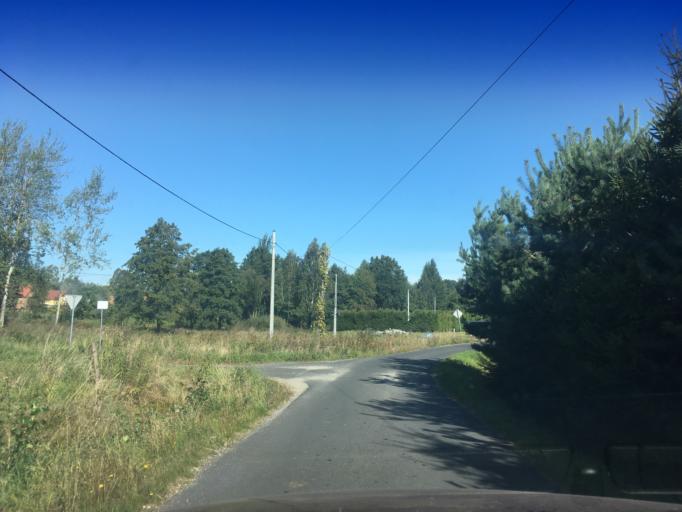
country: PL
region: Lower Silesian Voivodeship
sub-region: Powiat lubanski
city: Lesna
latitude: 51.0024
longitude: 15.1924
